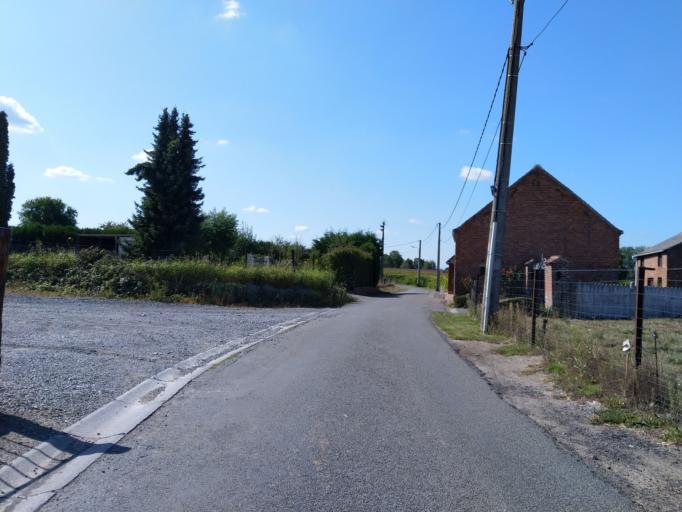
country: BE
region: Wallonia
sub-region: Province du Hainaut
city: Jurbise
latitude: 50.5266
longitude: 3.8710
